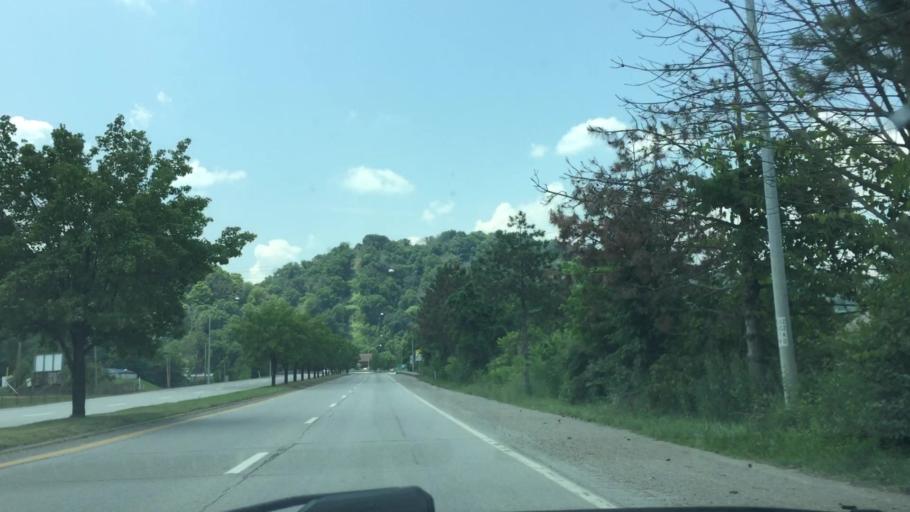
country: US
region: West Virginia
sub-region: Marshall County
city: Moundsville
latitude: 39.9070
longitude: -80.7543
